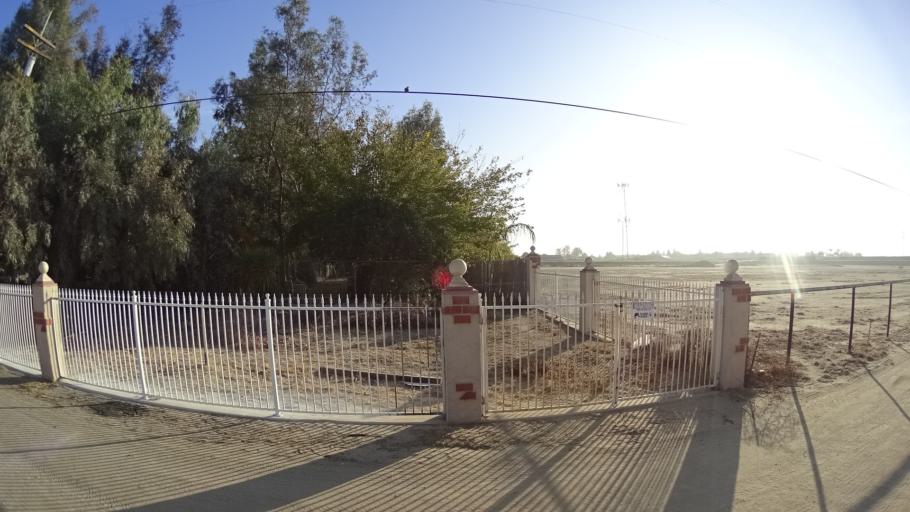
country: US
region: California
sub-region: Kern County
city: Greenacres
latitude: 35.4289
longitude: -119.1234
